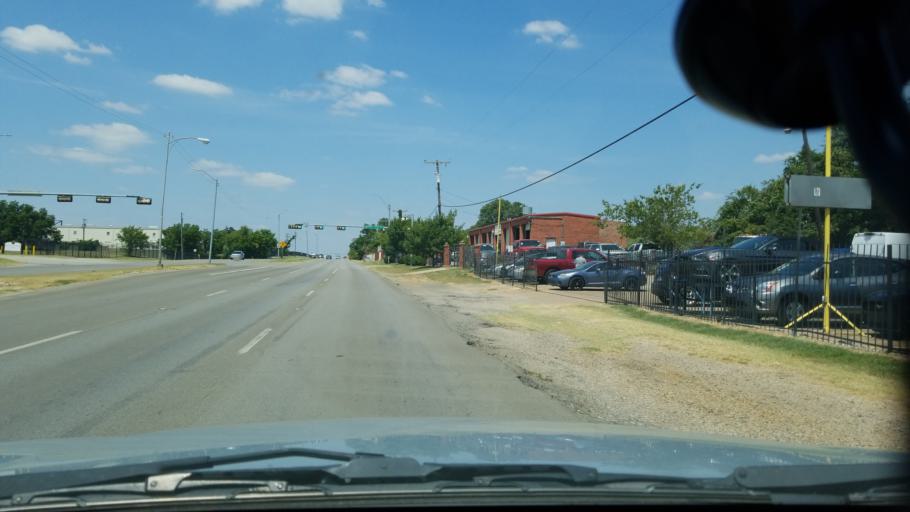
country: US
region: Texas
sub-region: Dallas County
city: Grand Prairie
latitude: 32.7463
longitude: -96.9621
